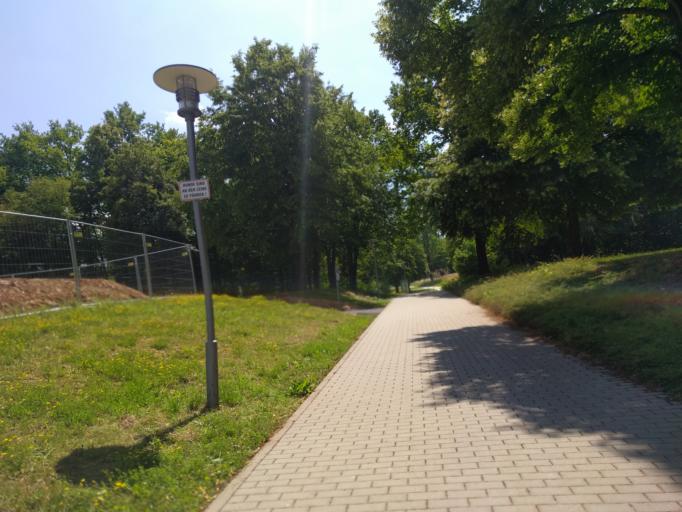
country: DE
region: Bavaria
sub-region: Upper Palatinate
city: Pentling
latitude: 48.9975
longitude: 12.0922
